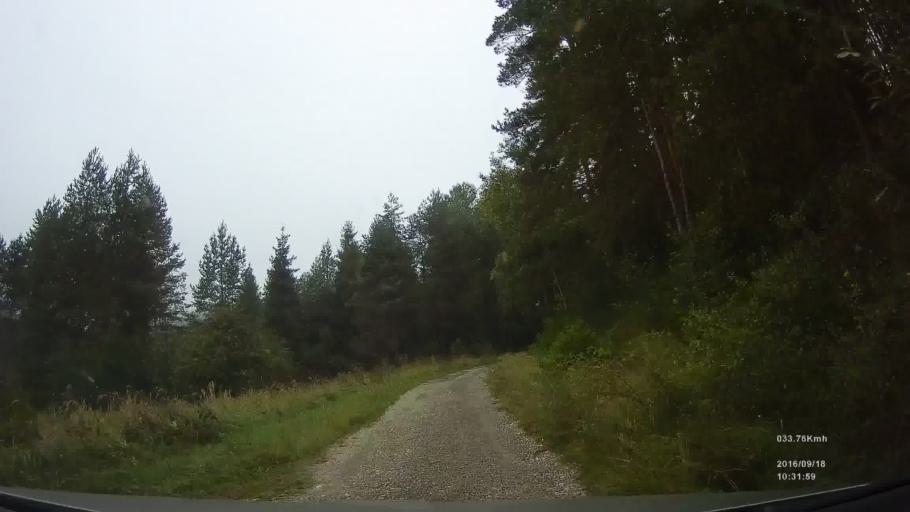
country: SK
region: Kosicky
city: Spisska Nova Ves
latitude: 48.9642
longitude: 20.6212
